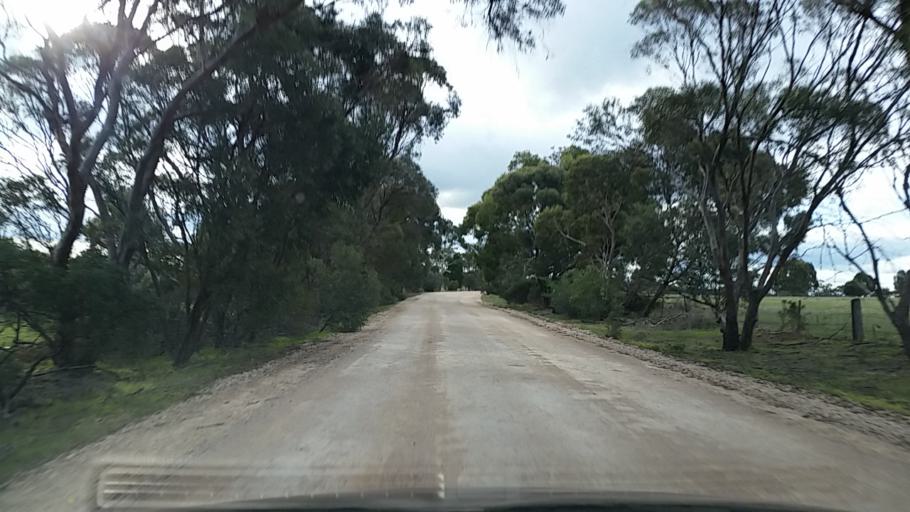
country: AU
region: South Australia
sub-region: Mount Barker
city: Callington
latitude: -34.9952
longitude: 139.0574
